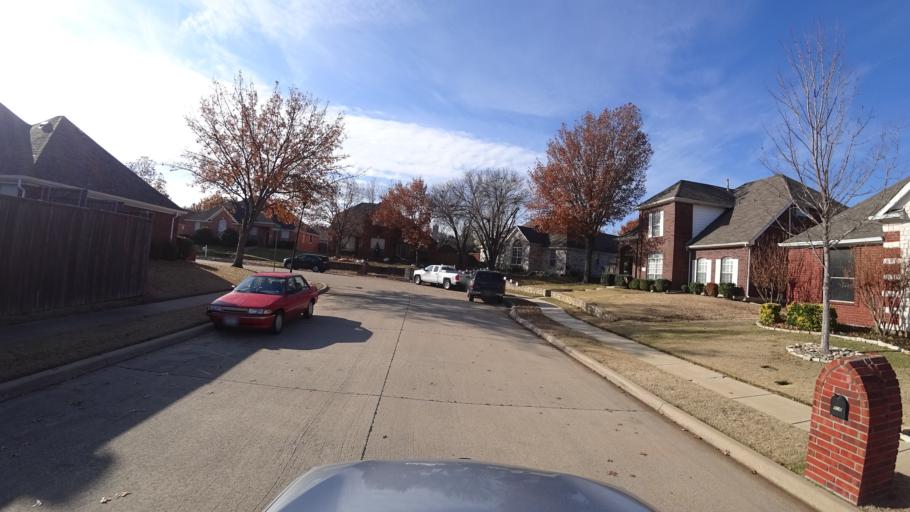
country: US
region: Texas
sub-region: Denton County
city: Lewisville
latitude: 33.0528
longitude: -97.0235
